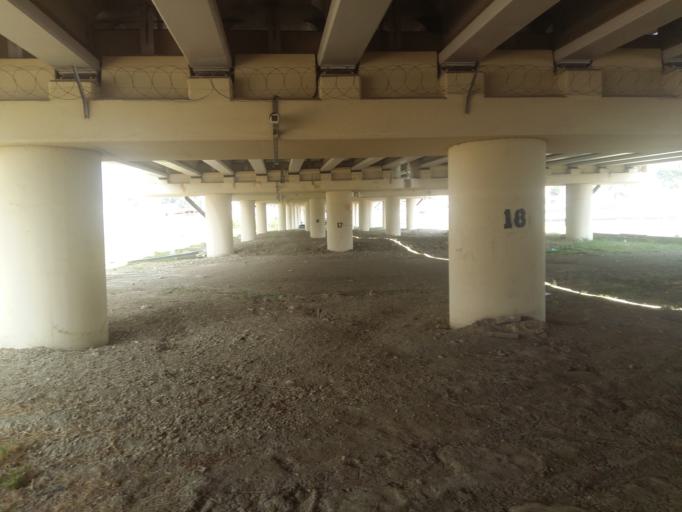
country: RU
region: Krasnodarskiy
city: Adler
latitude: 43.4119
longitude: 39.9667
